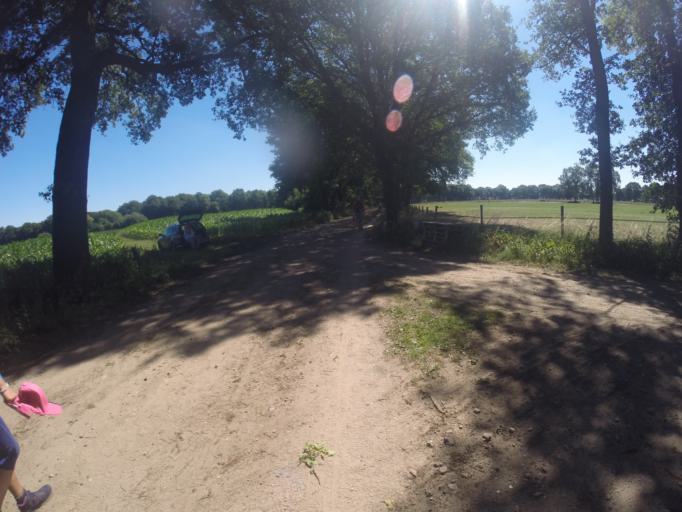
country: NL
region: Gelderland
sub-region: Gemeente Lochem
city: Lochem
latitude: 52.1339
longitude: 6.4176
